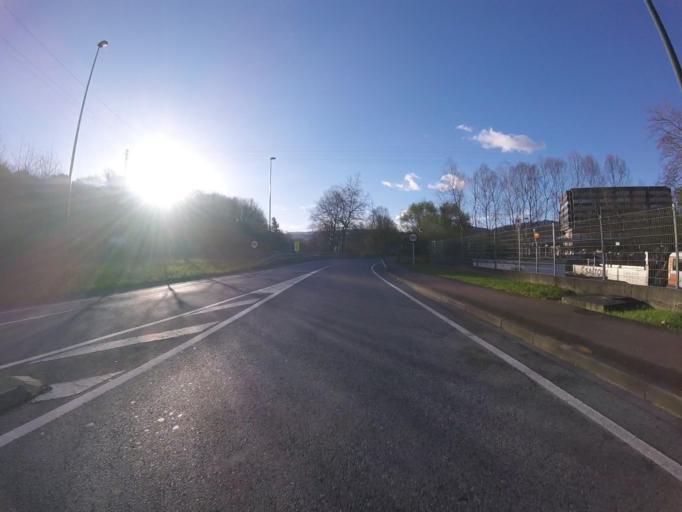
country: ES
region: Basque Country
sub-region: Provincia de Guipuzcoa
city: Errenteria
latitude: 43.3034
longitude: -1.8831
